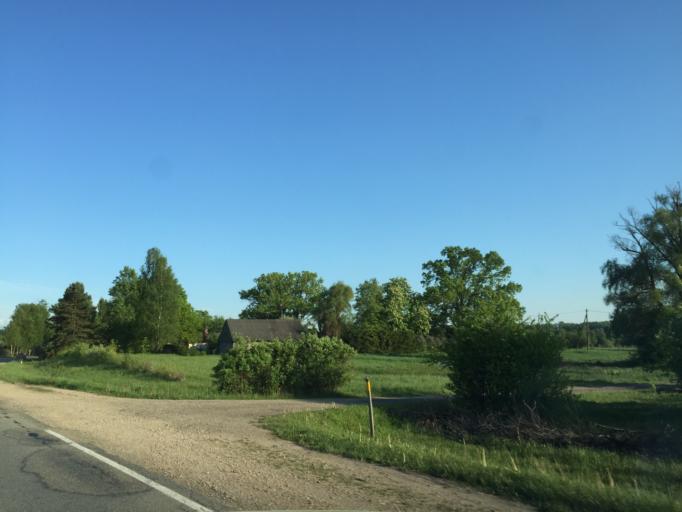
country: LV
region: Kekava
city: Kekava
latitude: 56.7890
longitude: 24.2934
